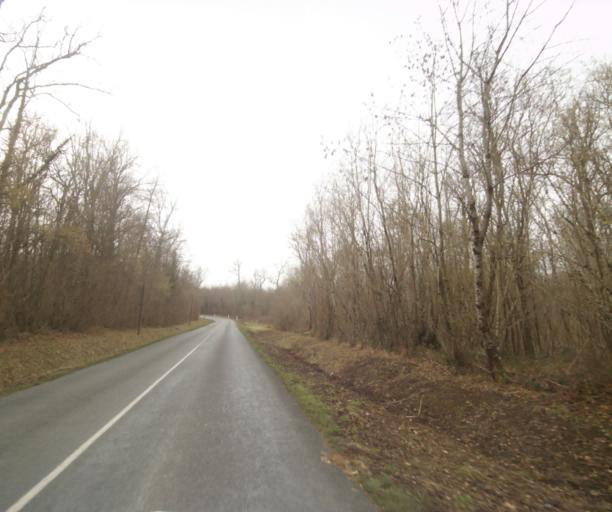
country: FR
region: Champagne-Ardenne
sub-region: Departement de la Haute-Marne
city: Villiers-en-Lieu
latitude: 48.6963
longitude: 4.8938
